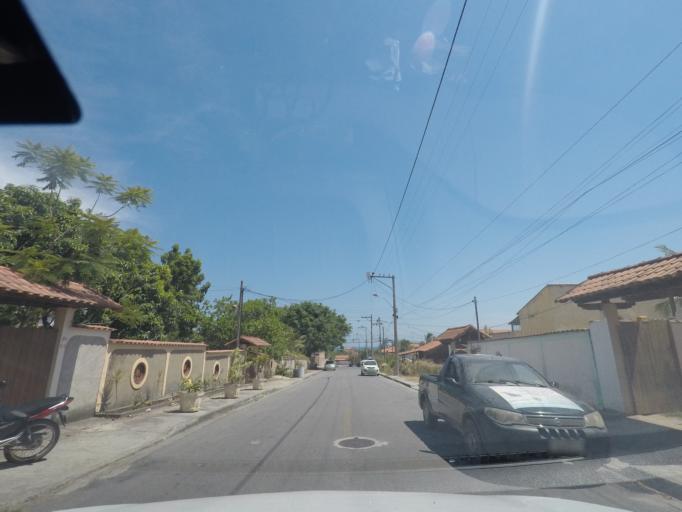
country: BR
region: Rio de Janeiro
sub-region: Marica
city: Marica
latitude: -22.9665
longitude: -42.9567
